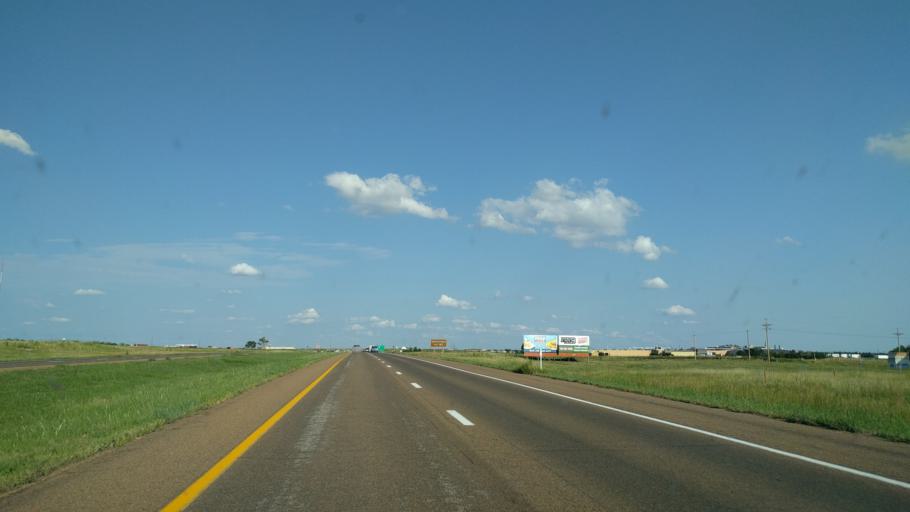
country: US
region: Kansas
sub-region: Ellis County
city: Hays
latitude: 38.9161
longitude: -99.3652
